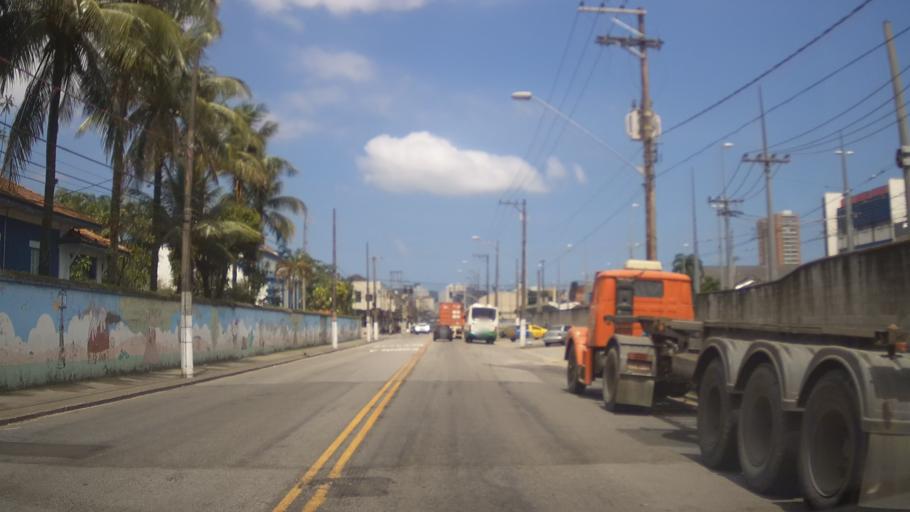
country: BR
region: Sao Paulo
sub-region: Santos
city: Santos
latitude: -23.9554
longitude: -46.3133
